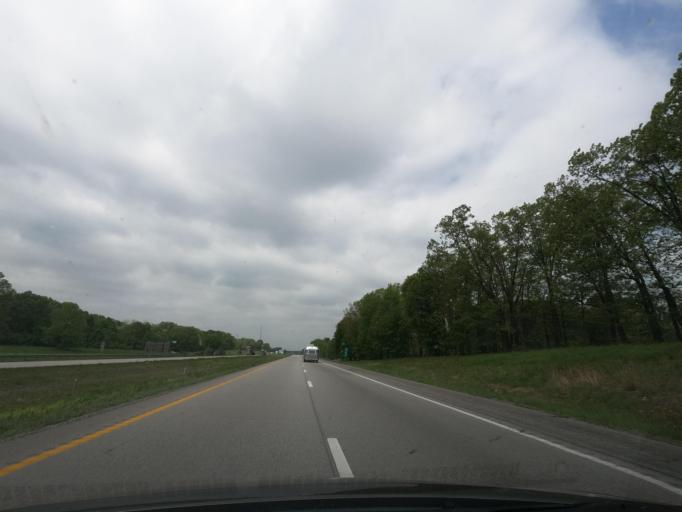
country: US
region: Missouri
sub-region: Jasper County
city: Duenweg
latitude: 37.0822
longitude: -94.3427
